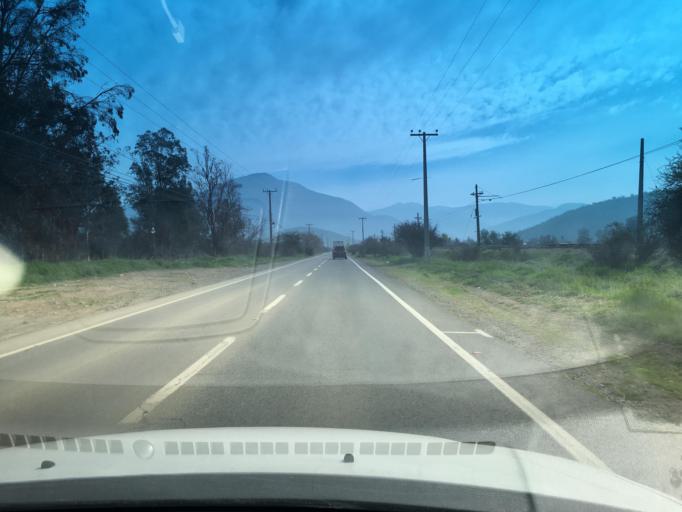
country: CL
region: Santiago Metropolitan
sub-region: Provincia de Chacabuco
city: Lampa
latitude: -33.1126
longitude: -70.9276
